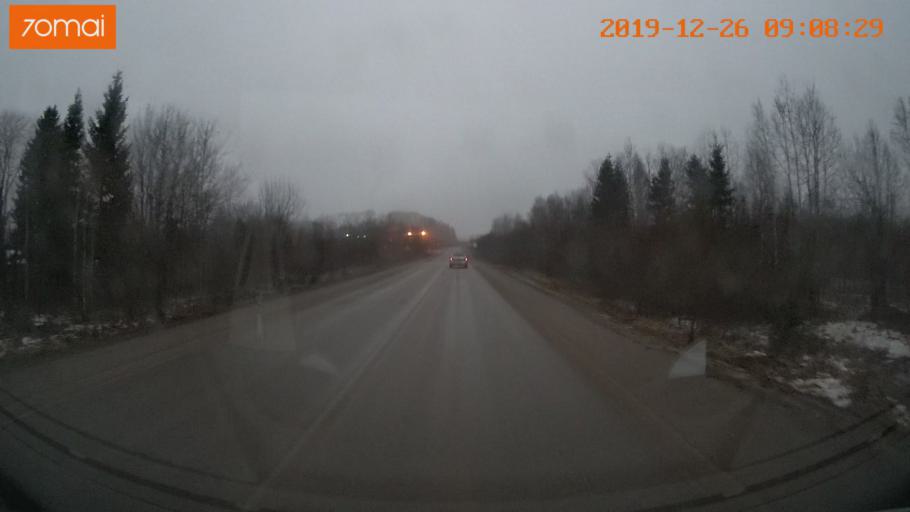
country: RU
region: Vologda
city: Gryazovets
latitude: 58.8571
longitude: 40.2485
